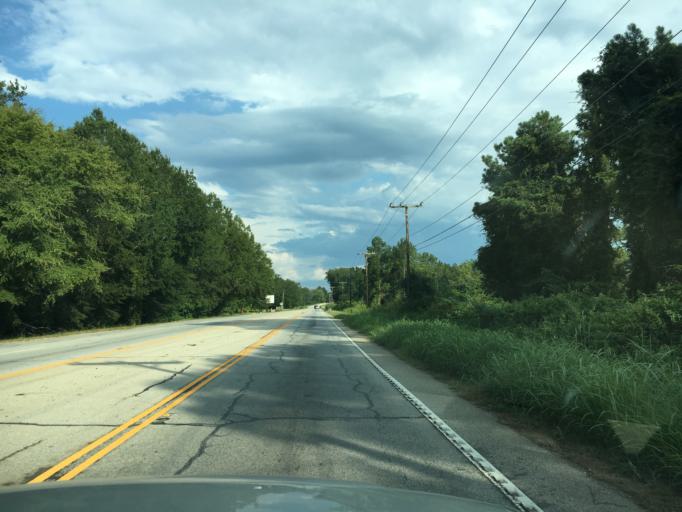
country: US
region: South Carolina
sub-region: Greenwood County
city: Ninety Six
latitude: 34.2377
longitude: -82.0683
